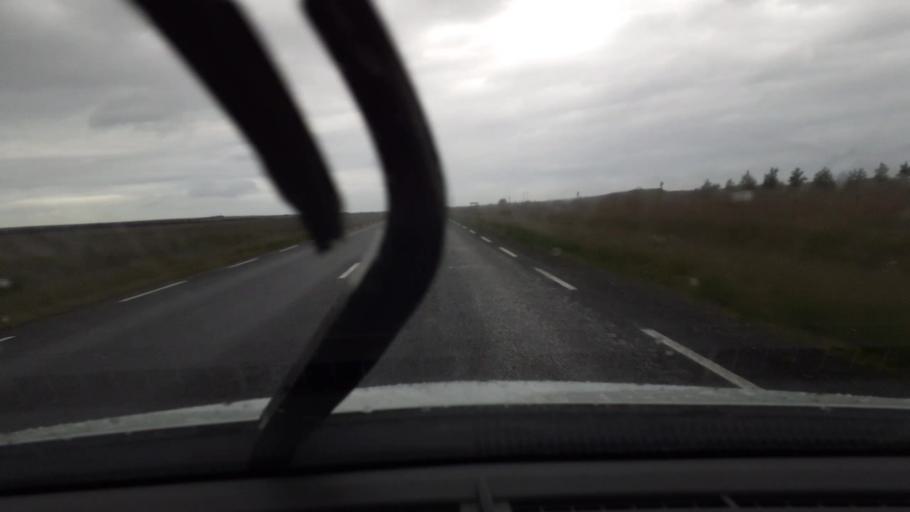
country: IS
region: West
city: Akranes
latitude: 64.3590
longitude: -21.9697
